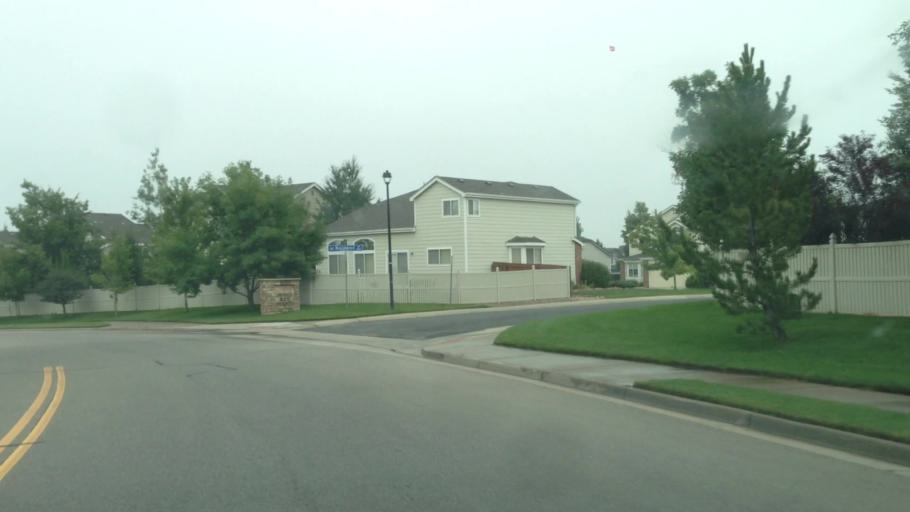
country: US
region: Colorado
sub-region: Douglas County
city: Parker
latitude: 39.6059
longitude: -104.7294
